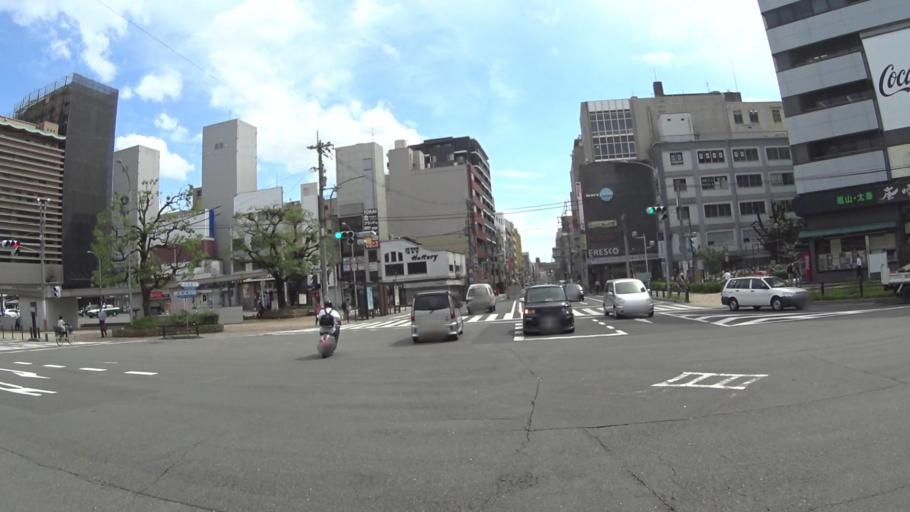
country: JP
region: Kyoto
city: Kyoto
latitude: 35.0038
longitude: 135.7488
